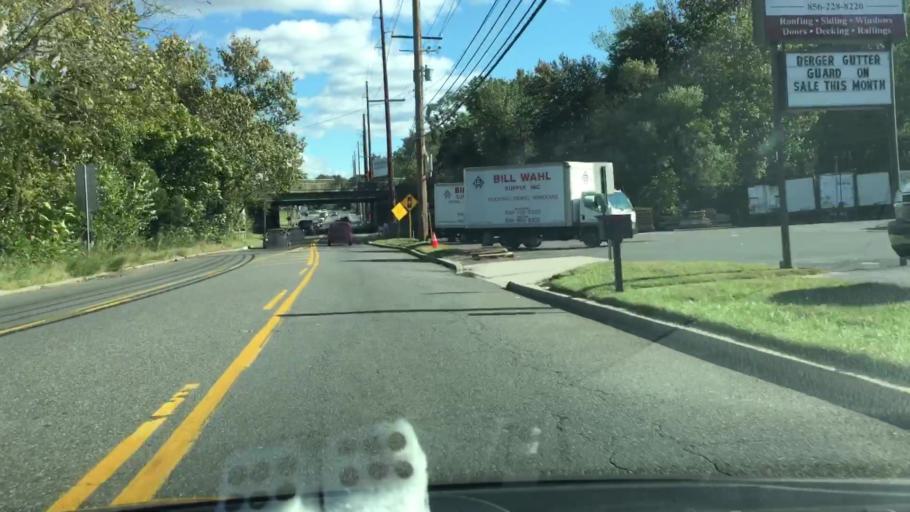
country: US
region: New Jersey
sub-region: Gloucester County
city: Turnersville
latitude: 39.7725
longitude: -75.0502
